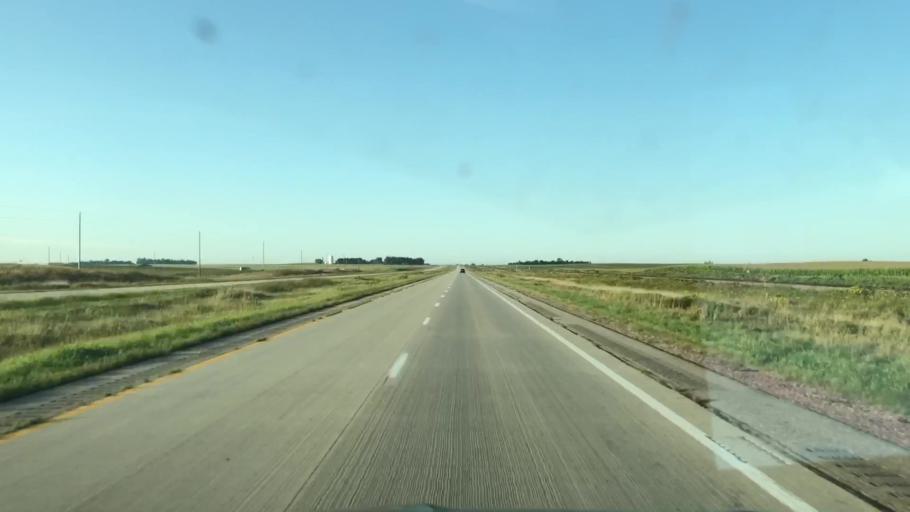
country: US
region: Iowa
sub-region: Osceola County
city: Sibley
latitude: 43.4808
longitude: -95.7038
